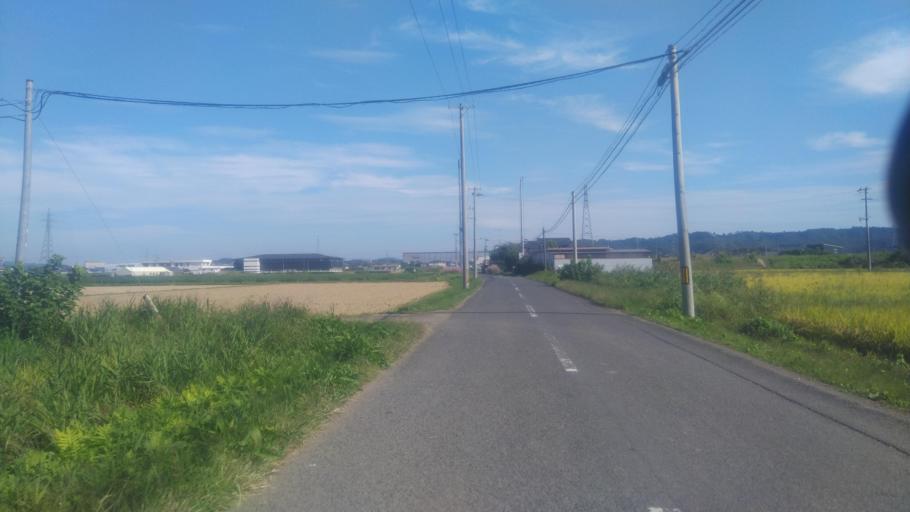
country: JP
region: Miyagi
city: Okawara
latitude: 38.0474
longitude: 140.7013
